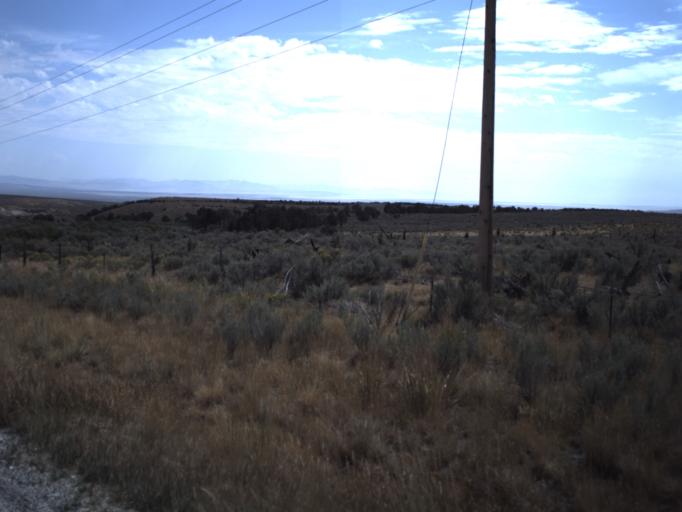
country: US
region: Idaho
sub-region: Cassia County
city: Burley
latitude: 41.8173
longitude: -113.2543
